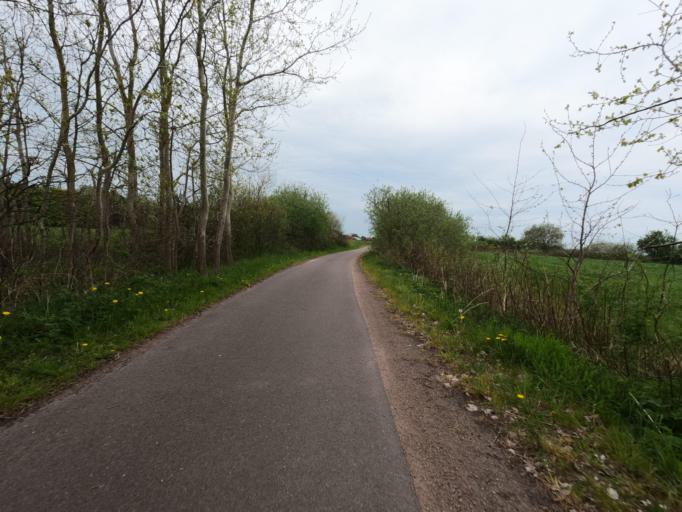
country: DE
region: Mecklenburg-Vorpommern
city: Born
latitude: 54.3467
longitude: 12.5551
